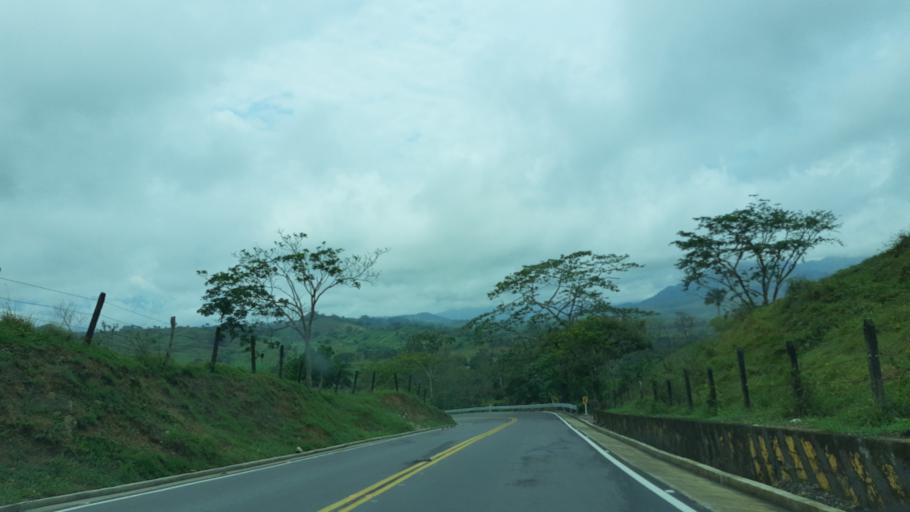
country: CO
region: Casanare
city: Sabanalarga
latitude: 4.7724
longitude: -73.0334
